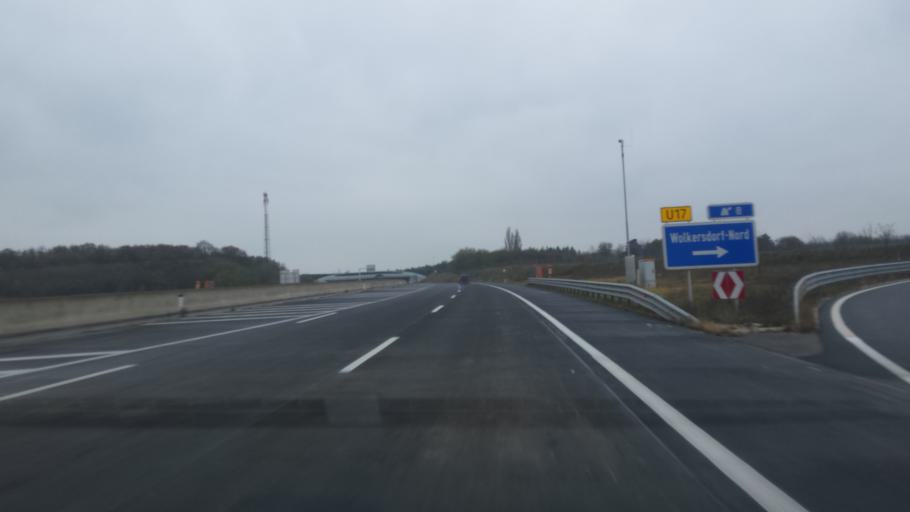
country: AT
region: Lower Austria
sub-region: Politischer Bezirk Mistelbach
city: Wolkersdorf im Weinviertel
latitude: 48.4022
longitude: 16.5284
